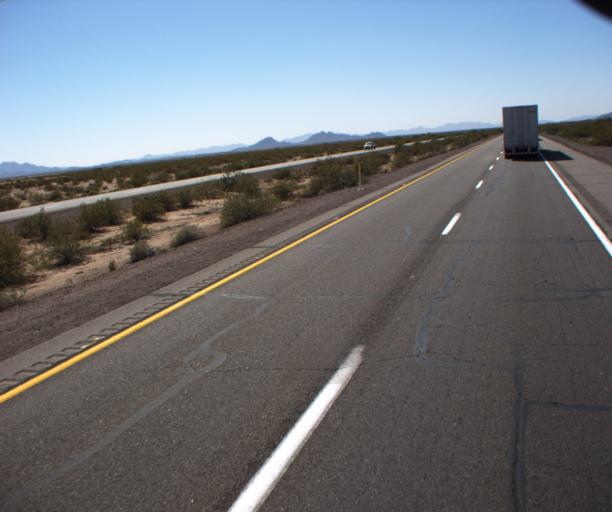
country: US
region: Arizona
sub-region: Yuma County
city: Wellton
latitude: 32.7093
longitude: -113.8505
